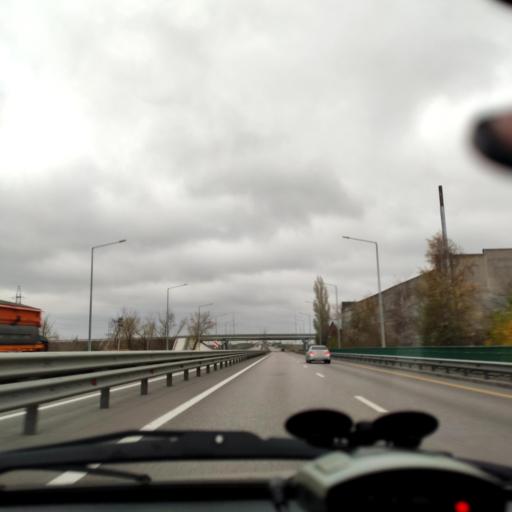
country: RU
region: Voronezj
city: Novaya Usman'
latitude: 51.6299
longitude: 39.3180
